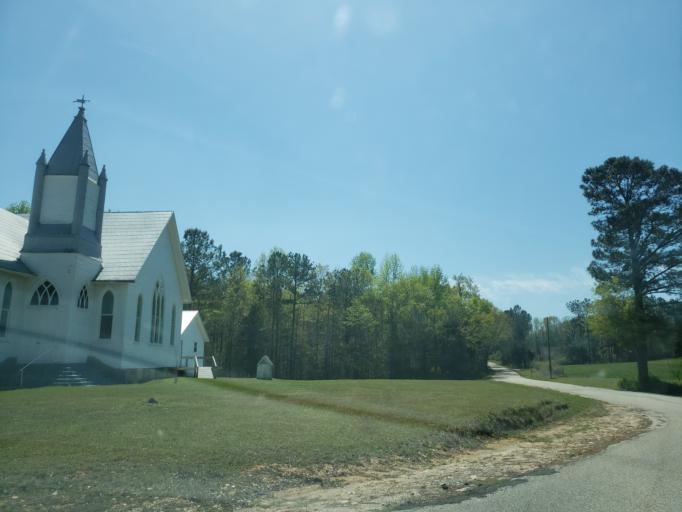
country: US
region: Alabama
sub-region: Tallapoosa County
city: Camp Hill
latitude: 32.6871
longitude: -85.6691
